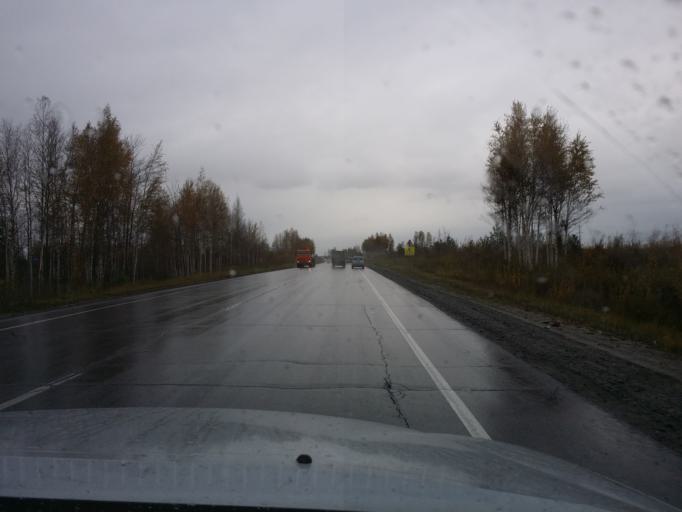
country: RU
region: Khanty-Mansiyskiy Avtonomnyy Okrug
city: Megion
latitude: 61.0670
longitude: 76.2558
